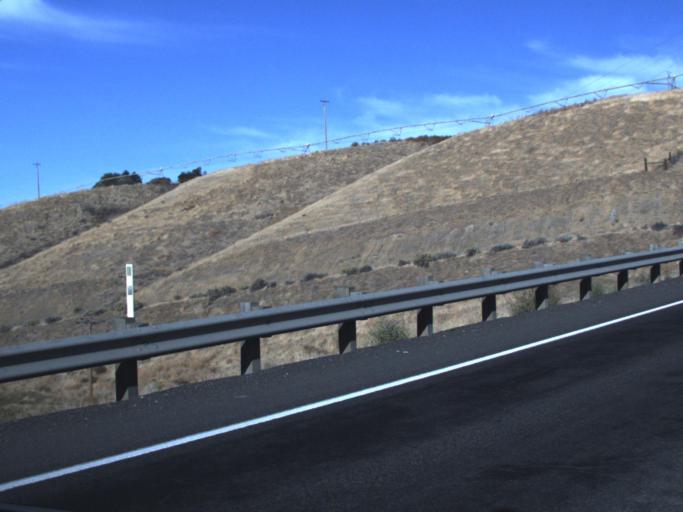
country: US
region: Washington
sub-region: Franklin County
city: Basin City
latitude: 46.5888
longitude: -119.0050
